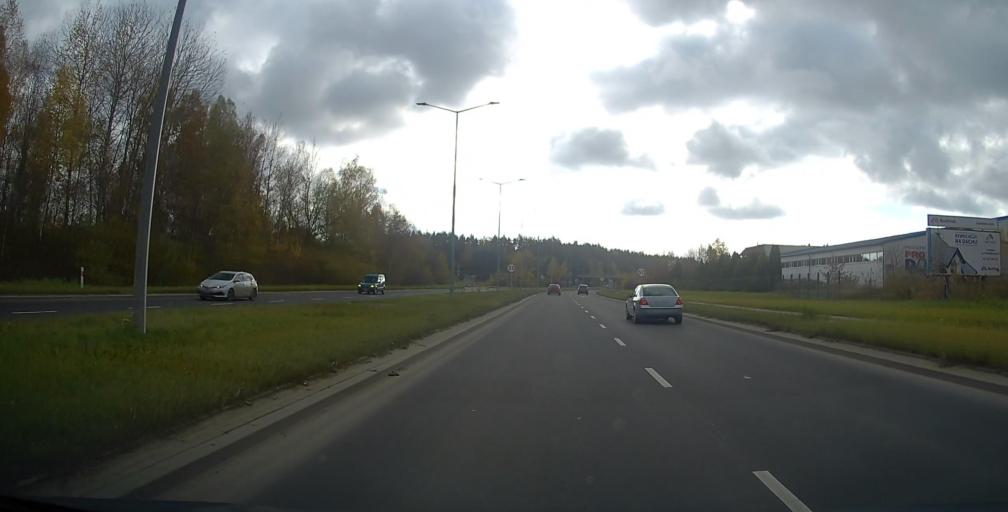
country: PL
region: Warmian-Masurian Voivodeship
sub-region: Powiat elcki
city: Elk
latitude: 53.8207
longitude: 22.3891
